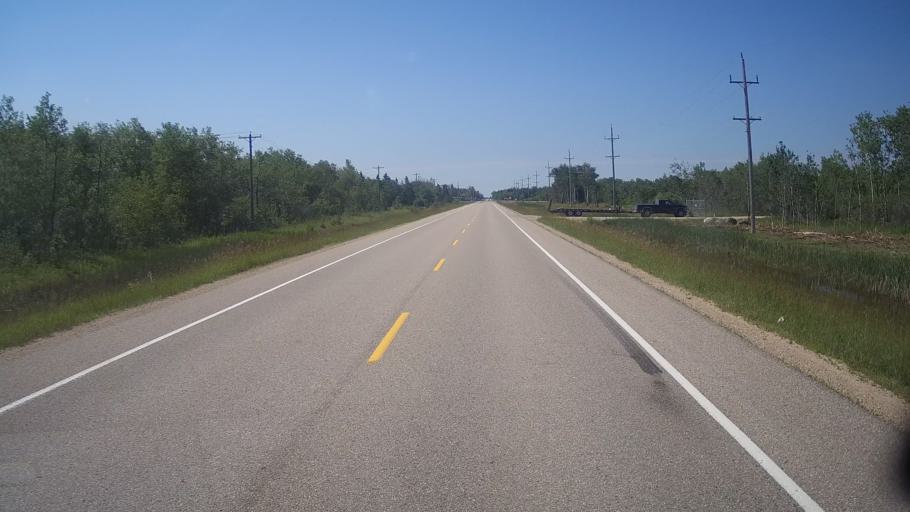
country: CA
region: Manitoba
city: La Broquerie
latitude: 49.6697
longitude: -96.4571
